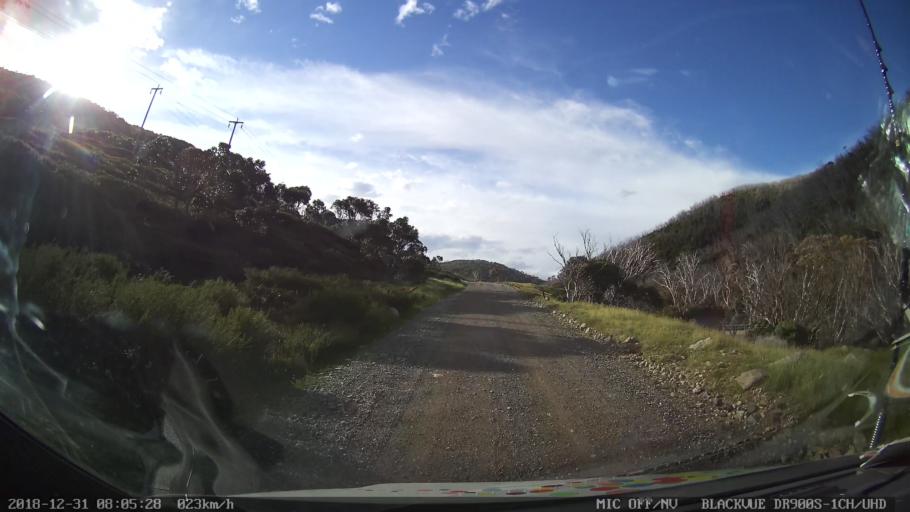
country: AU
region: New South Wales
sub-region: Snowy River
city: Jindabyne
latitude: -36.3712
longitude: 148.4065
